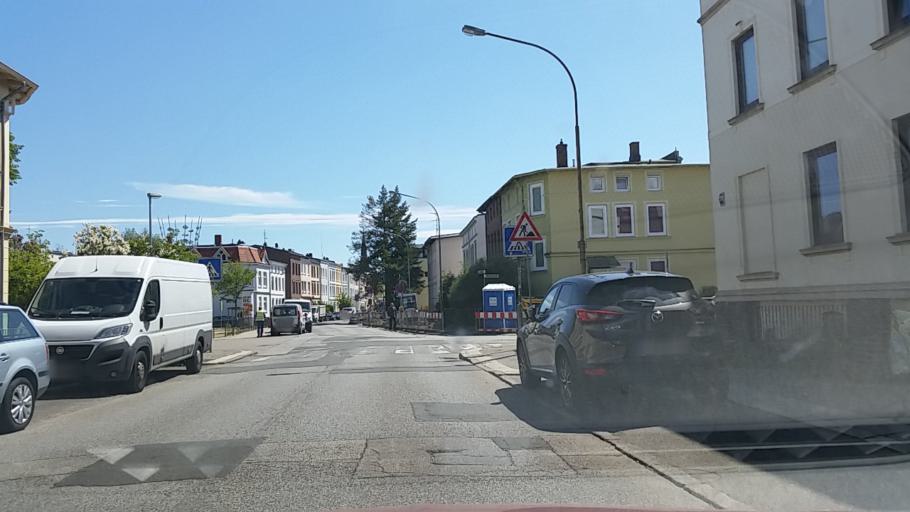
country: DE
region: Schleswig-Holstein
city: Luebeck
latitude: 53.8759
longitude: 10.6702
